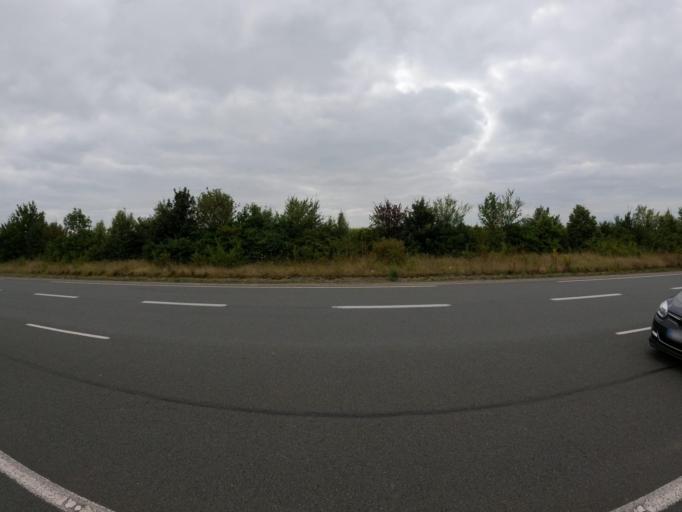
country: FR
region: Poitou-Charentes
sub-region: Departement des Deux-Sevres
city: Vouille
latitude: 46.3073
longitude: -0.3695
